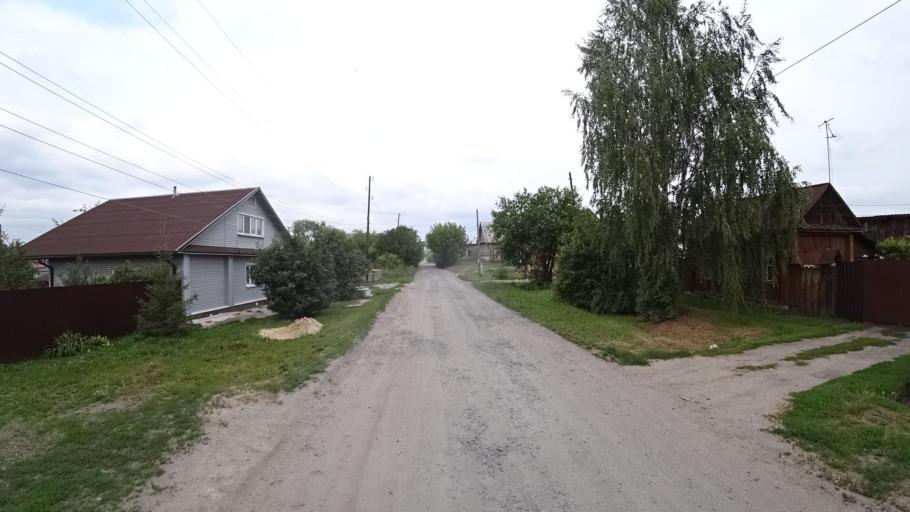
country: RU
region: Sverdlovsk
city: Kamyshlov
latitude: 56.8484
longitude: 62.6801
